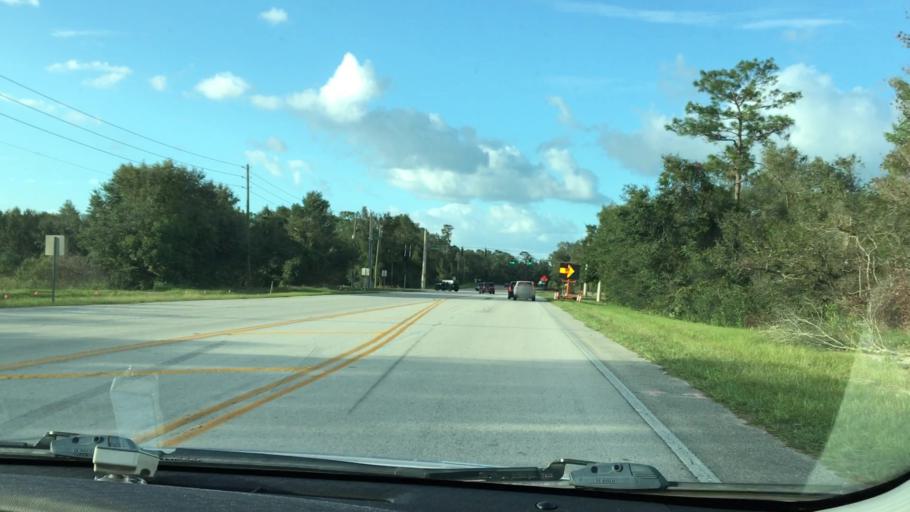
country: US
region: Florida
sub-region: Volusia County
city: Orange City
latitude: 28.9326
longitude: -81.2819
